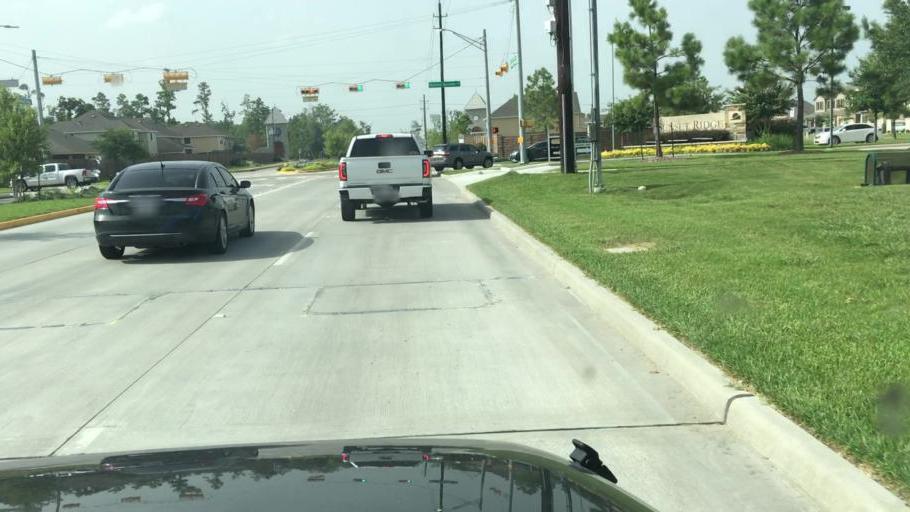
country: US
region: Texas
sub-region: Harris County
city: Atascocita
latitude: 29.9392
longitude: -95.2114
